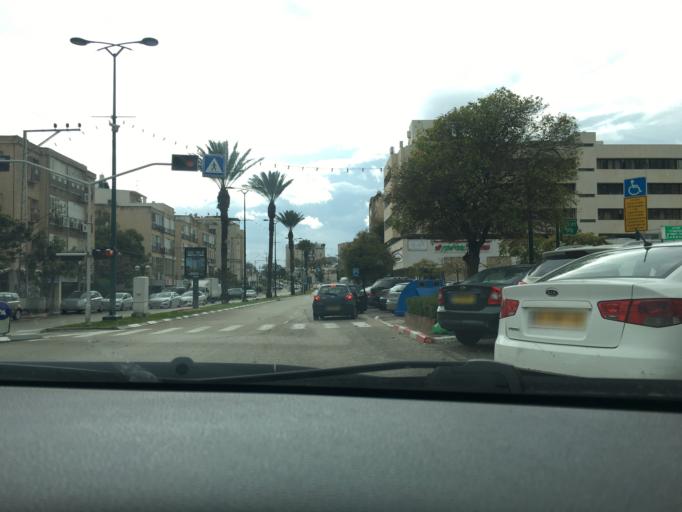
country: IL
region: Tel Aviv
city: Ramat HaSharon
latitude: 32.1392
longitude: 34.8419
